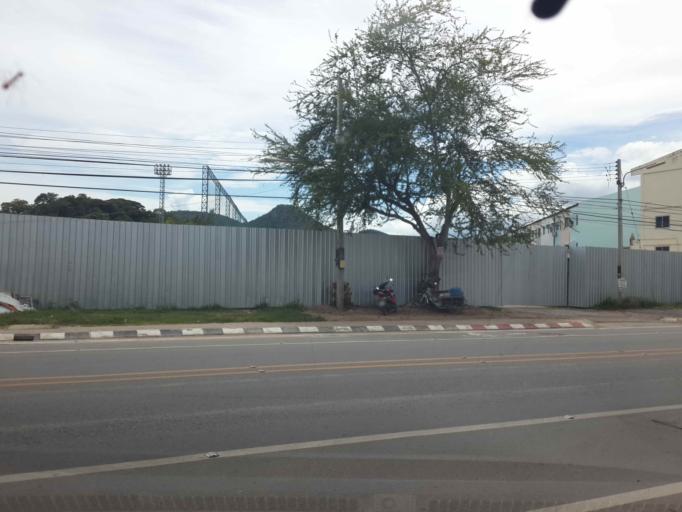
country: TH
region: Prachuap Khiri Khan
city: Hua Hin
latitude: 12.5280
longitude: 99.9700
